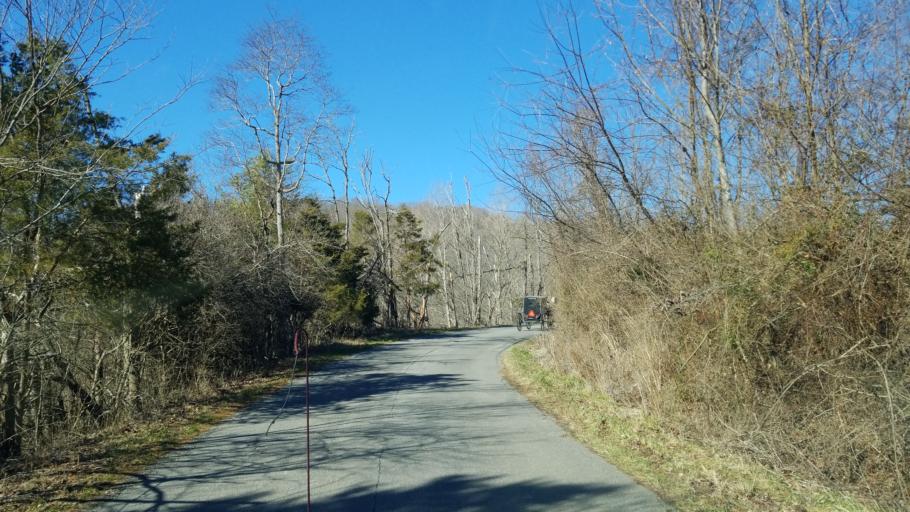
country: US
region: Virginia
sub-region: Pulaski County
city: Pulaski
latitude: 37.1620
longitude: -80.8582
